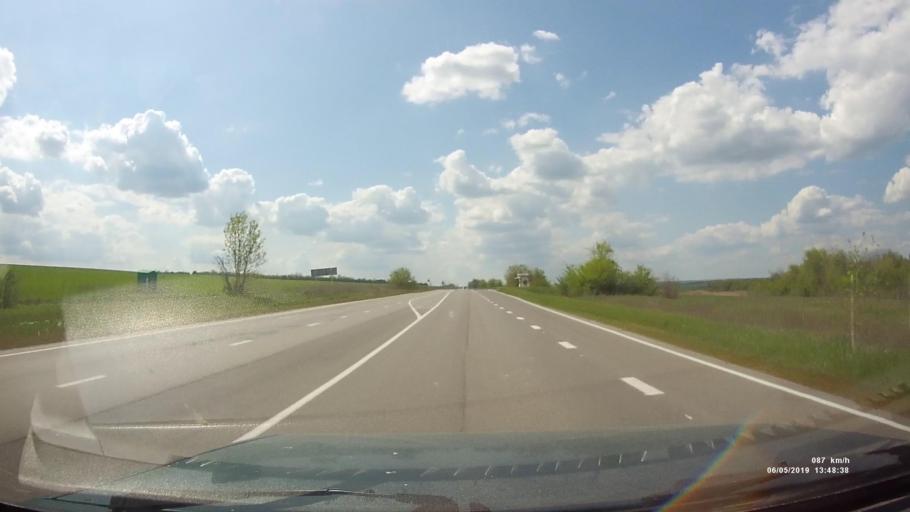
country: RU
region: Rostov
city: Melikhovskaya
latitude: 47.6585
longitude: 40.5397
